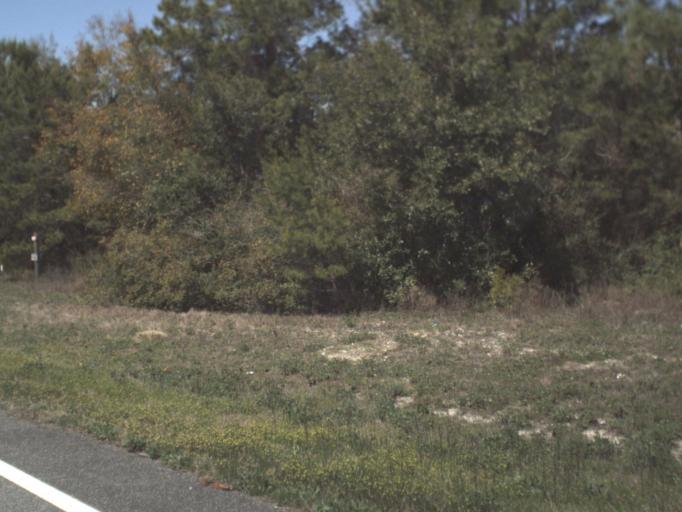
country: US
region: Florida
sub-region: Franklin County
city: Carrabelle
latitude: 29.9303
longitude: -84.4367
